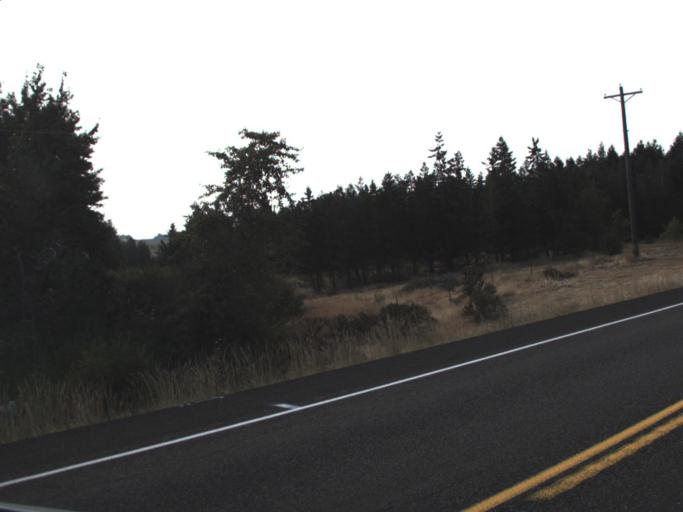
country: US
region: Washington
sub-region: Kittitas County
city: Ellensburg
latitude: 47.1116
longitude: -120.6656
